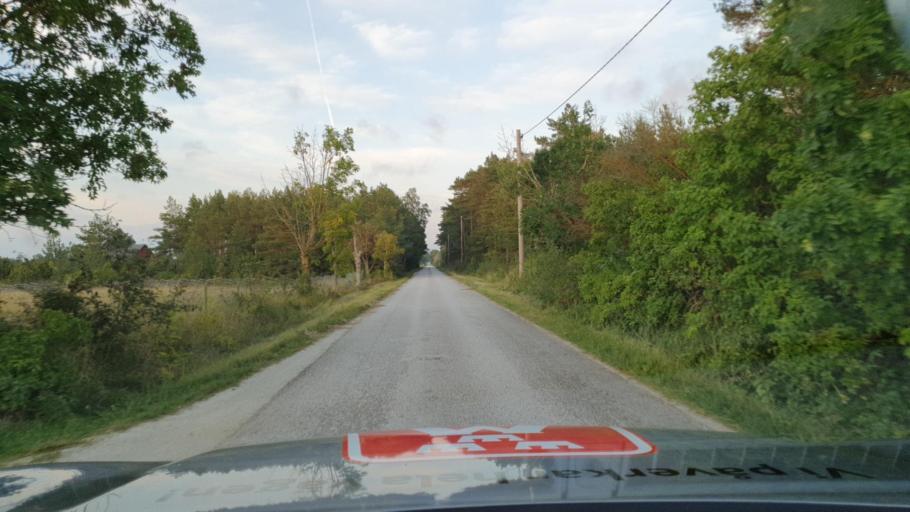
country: SE
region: Gotland
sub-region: Gotland
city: Klintehamn
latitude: 57.2753
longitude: 18.1348
